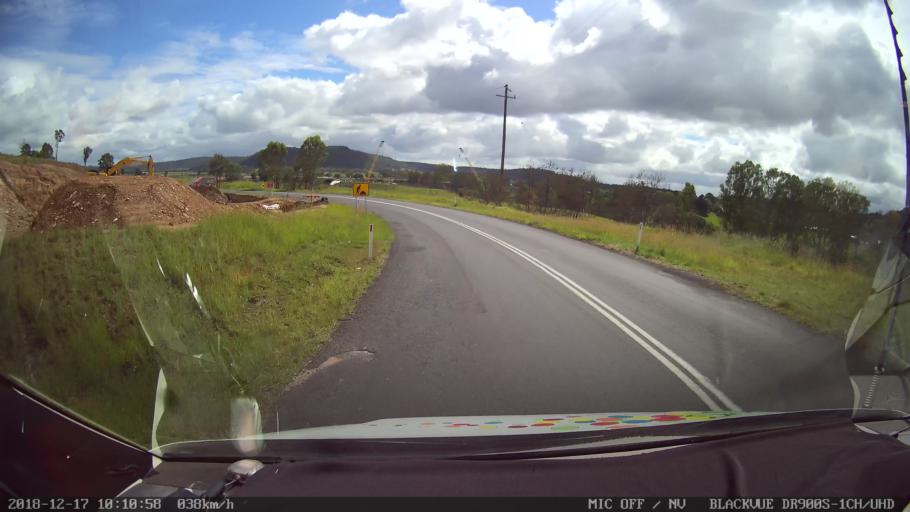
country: AU
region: New South Wales
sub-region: Clarence Valley
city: Gordon
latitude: -28.8886
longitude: 152.5600
